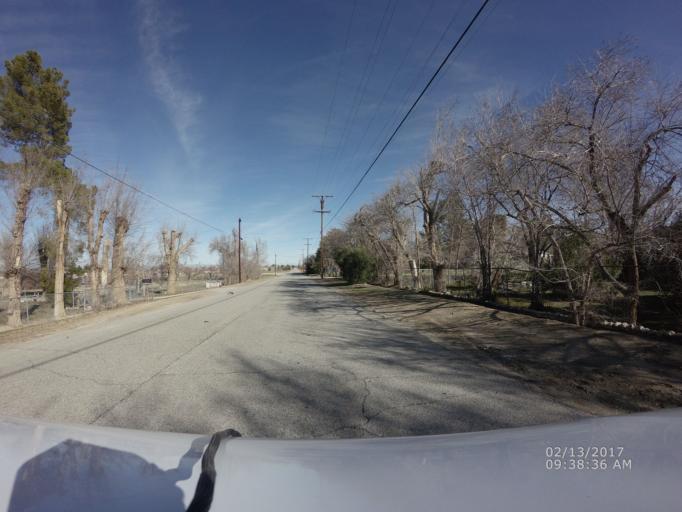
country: US
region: California
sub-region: Los Angeles County
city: Littlerock
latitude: 34.5458
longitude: -117.9669
